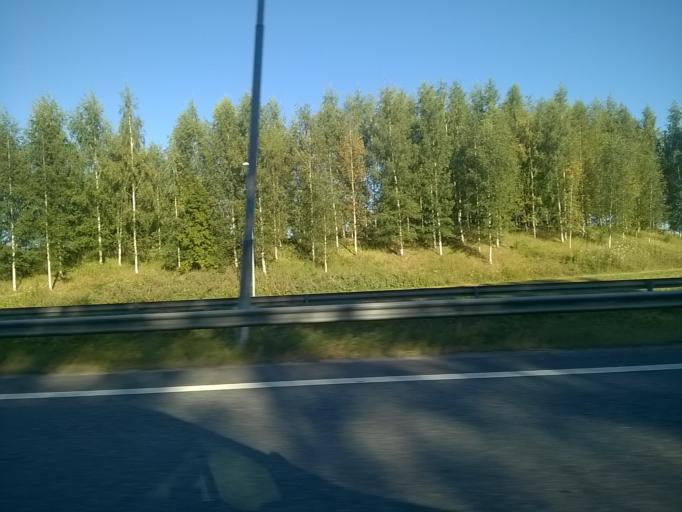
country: FI
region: Pirkanmaa
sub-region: Tampere
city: Tampere
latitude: 61.4869
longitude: 23.8740
